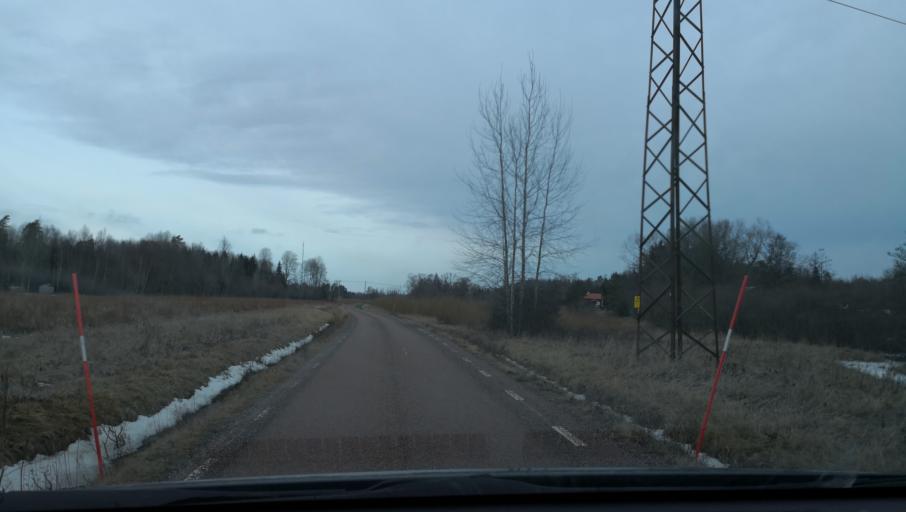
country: SE
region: Vaestmanland
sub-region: Vasteras
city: Skultuna
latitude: 59.6074
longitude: 16.4117
